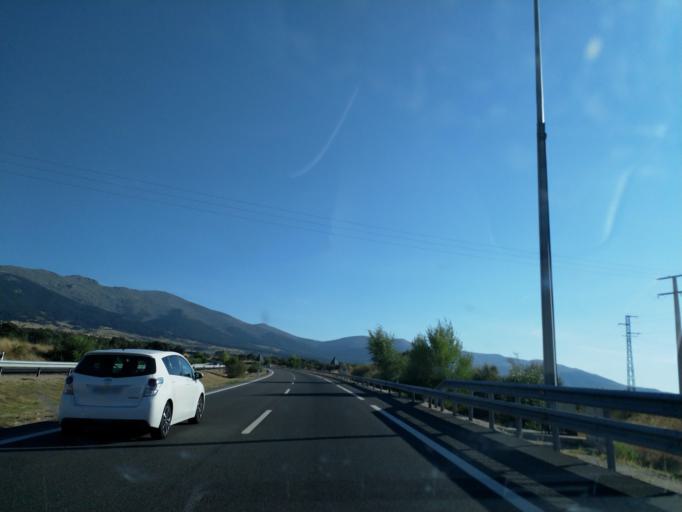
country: ES
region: Castille and Leon
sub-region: Provincia de Segovia
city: Ortigosa del Monte
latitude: 40.8701
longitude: -4.1227
